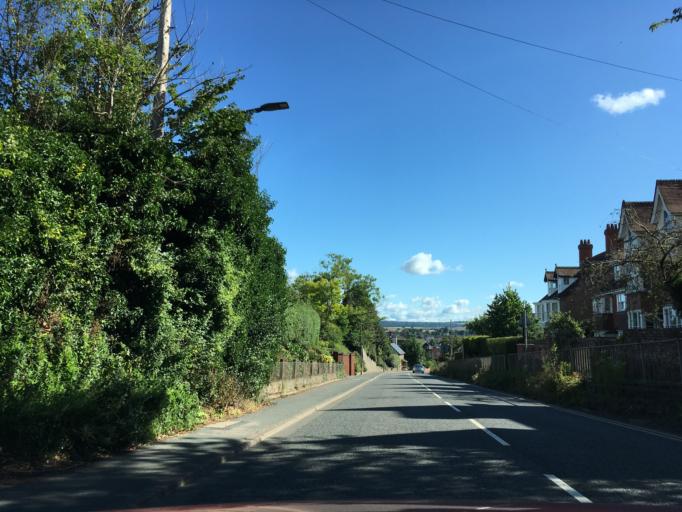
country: GB
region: England
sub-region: Herefordshire
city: Ross on Wye
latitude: 51.9110
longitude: -2.5856
